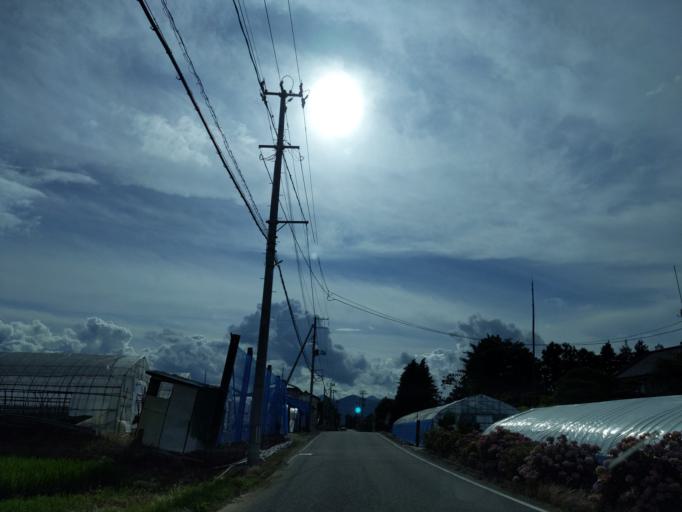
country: JP
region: Fukushima
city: Koriyama
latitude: 37.3455
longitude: 140.3168
